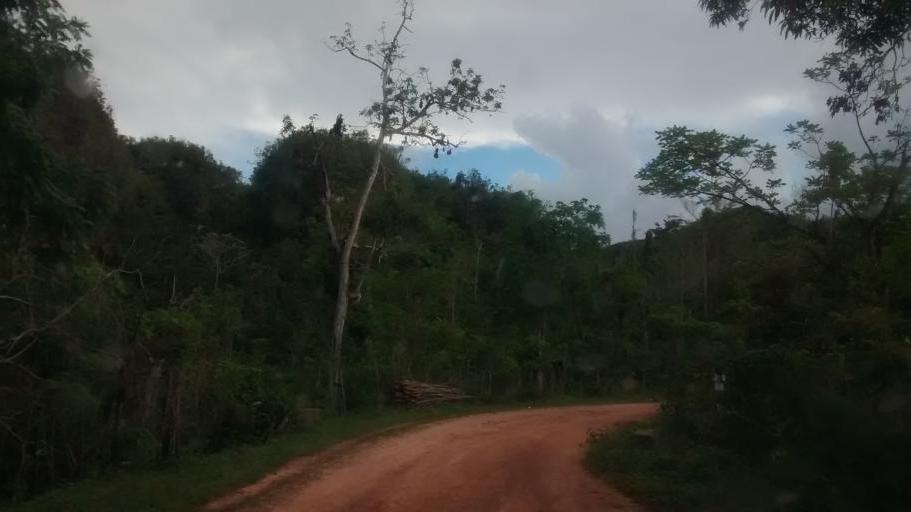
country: HT
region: Grandans
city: Corail
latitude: 18.5167
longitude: -73.7850
